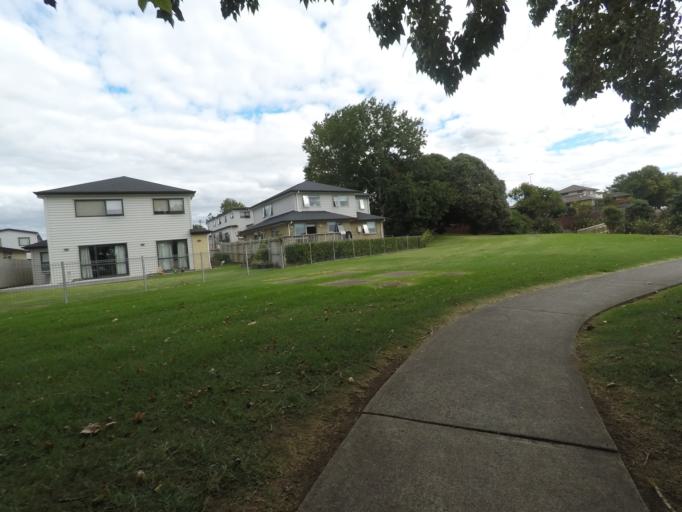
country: NZ
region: Auckland
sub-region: Auckland
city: Papakura
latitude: -37.0600
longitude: 174.9372
